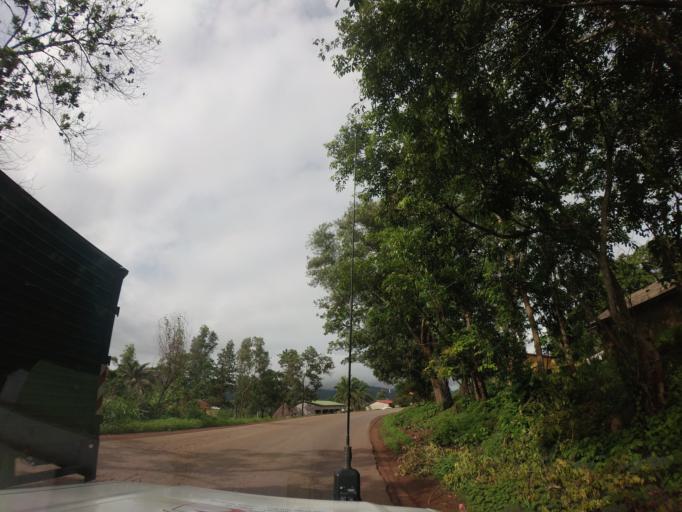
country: GN
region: Kindia
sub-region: Coyah
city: Coyah
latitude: 9.8030
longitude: -13.2838
